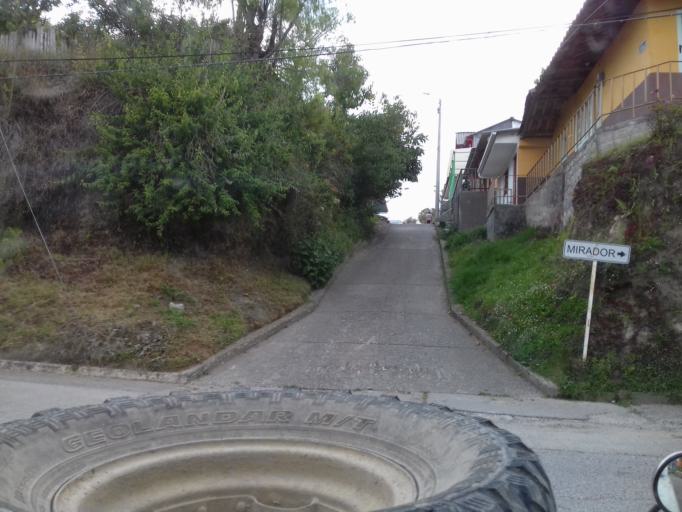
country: CO
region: Quindio
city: Salento
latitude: 4.6401
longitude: -75.5684
